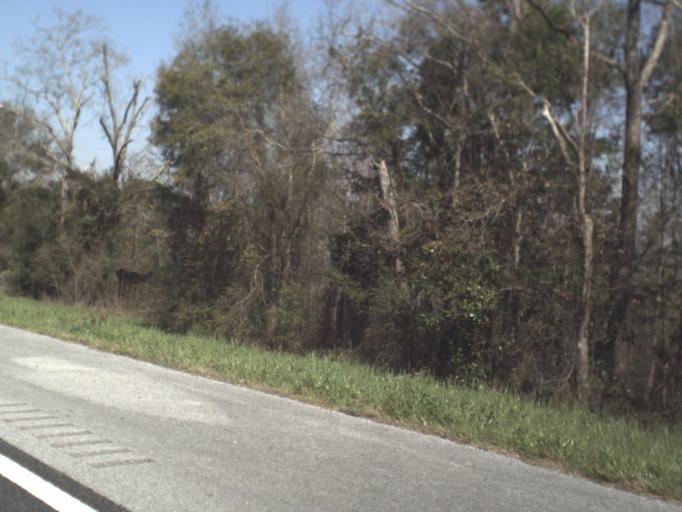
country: US
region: Florida
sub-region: Jackson County
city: Sneads
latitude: 30.6507
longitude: -85.0164
